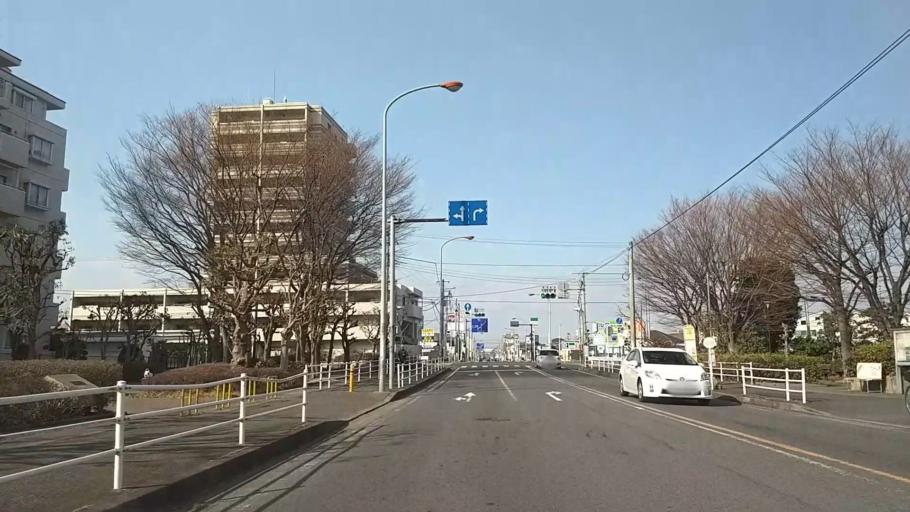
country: JP
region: Kanagawa
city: Chigasaki
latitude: 35.3396
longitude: 139.4132
